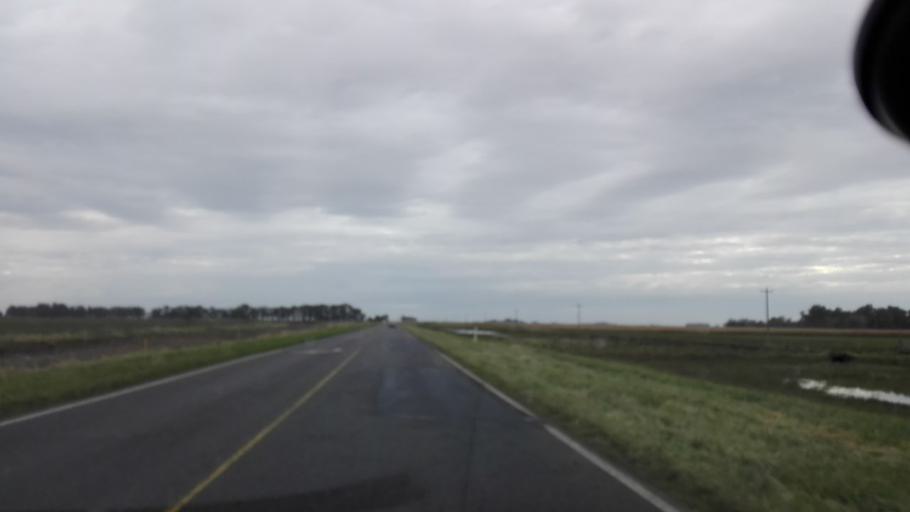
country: AR
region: Buenos Aires
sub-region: Partido de Rauch
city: Rauch
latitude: -36.5942
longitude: -59.0563
